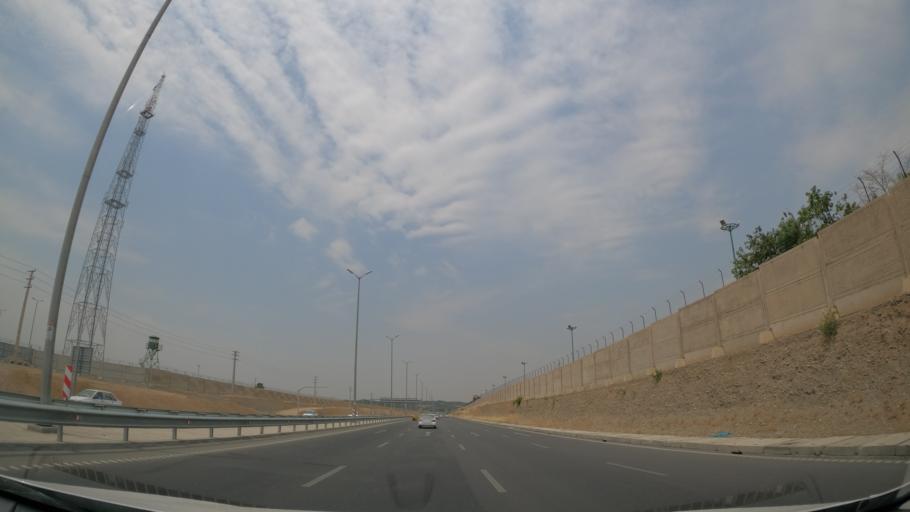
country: IR
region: Tehran
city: Shahr-e Qods
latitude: 35.7407
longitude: 51.2360
